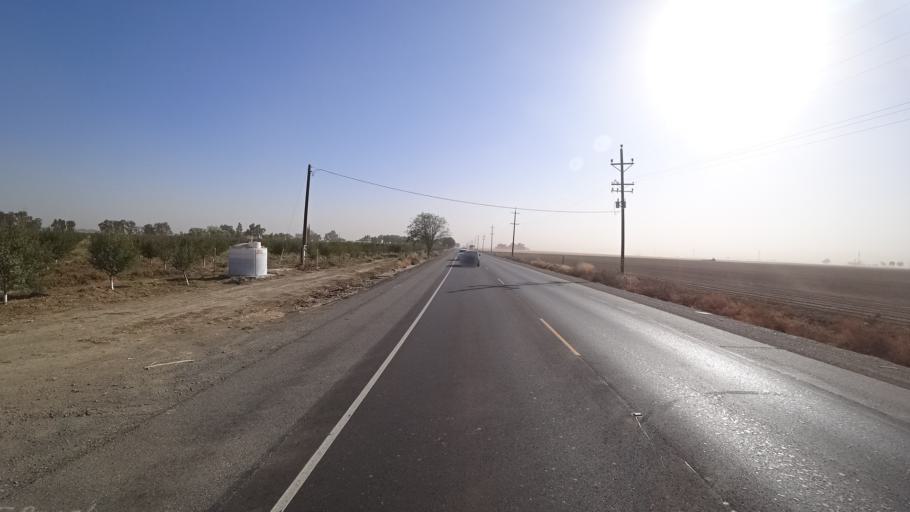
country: US
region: California
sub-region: Yolo County
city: Woodland
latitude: 38.7882
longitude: -121.7282
